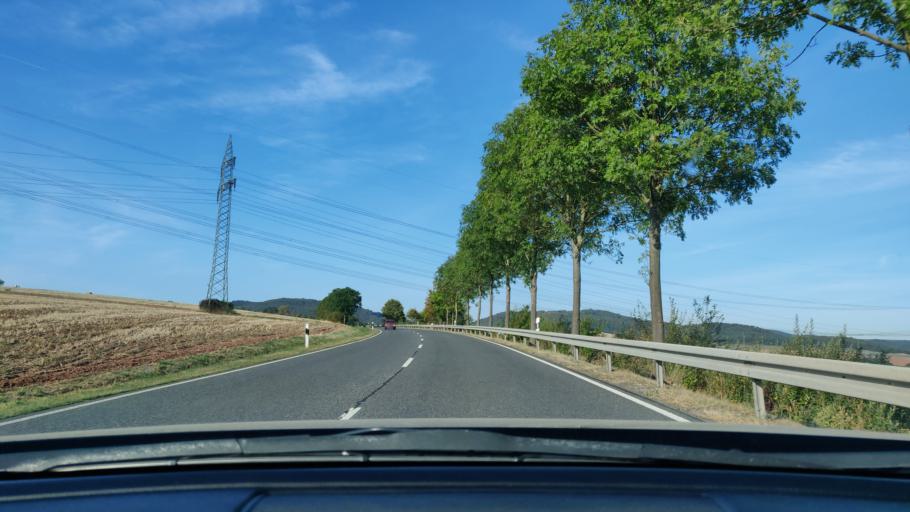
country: DE
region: Hesse
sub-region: Regierungsbezirk Kassel
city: Bad Wildungen
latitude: 51.1332
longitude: 9.1401
